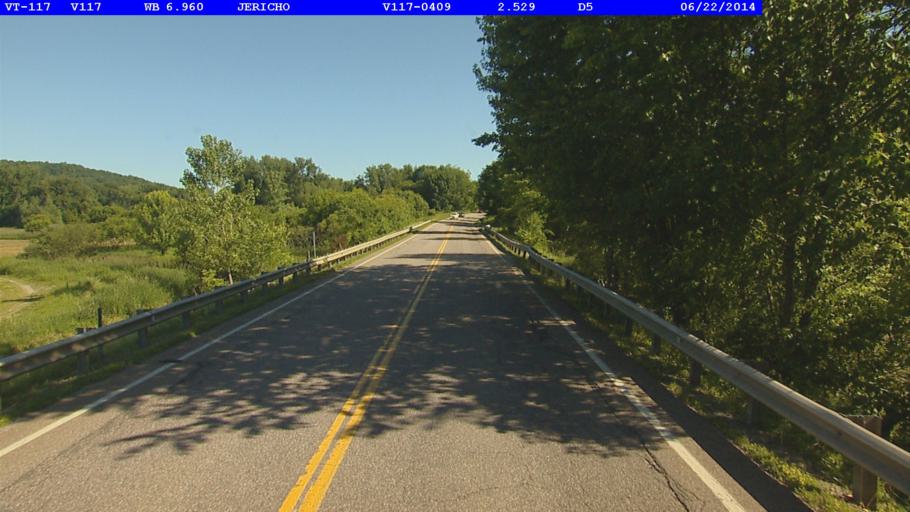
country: US
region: Vermont
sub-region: Chittenden County
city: Williston
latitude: 44.4393
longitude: -73.0198
